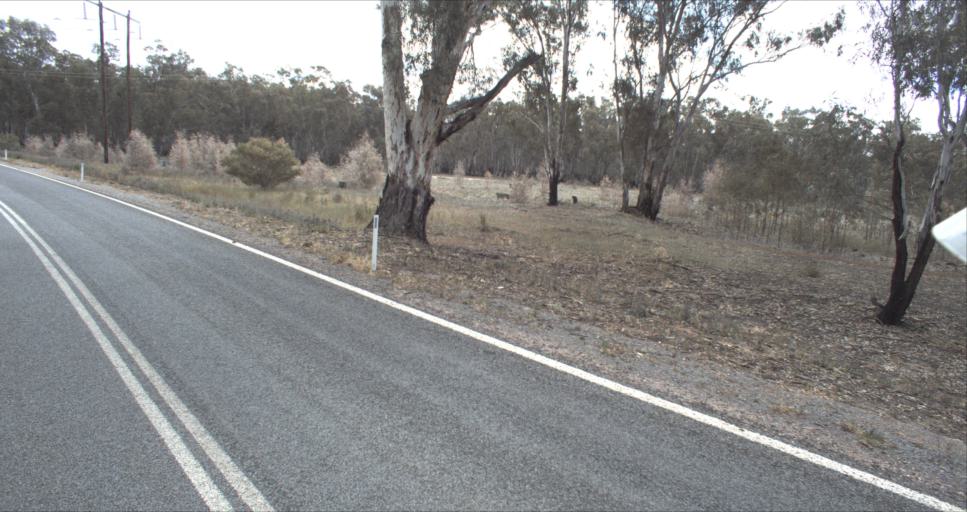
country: AU
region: New South Wales
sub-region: Leeton
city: Leeton
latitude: -34.6235
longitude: 146.3832
